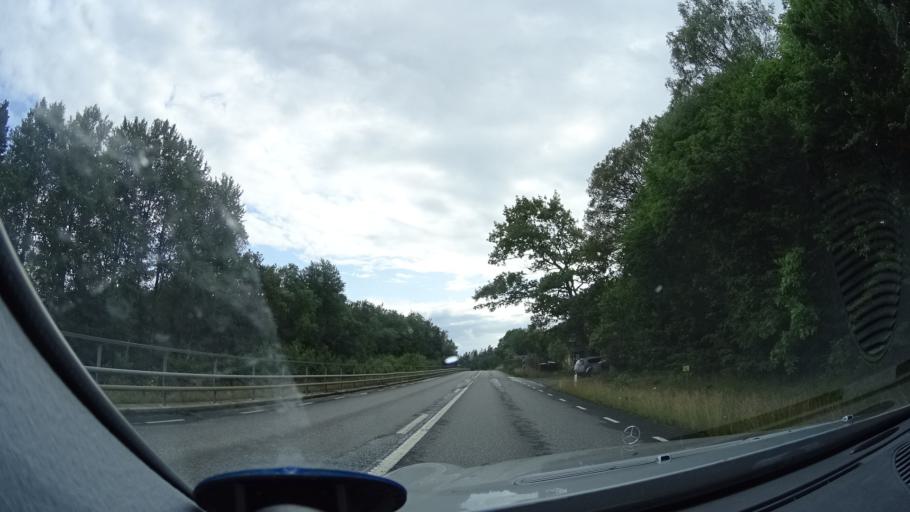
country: SE
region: Blekinge
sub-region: Karlshamns Kommun
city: Svangsta
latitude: 56.2606
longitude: 14.8392
